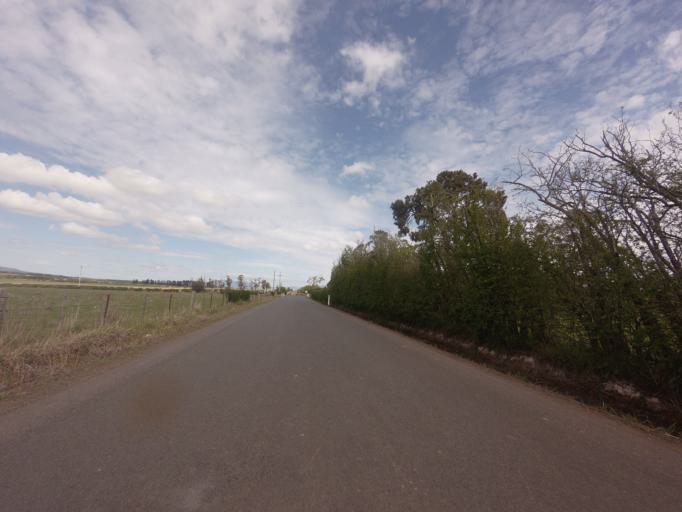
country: AU
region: Tasmania
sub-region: Northern Midlands
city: Longford
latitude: -41.6244
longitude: 147.1282
